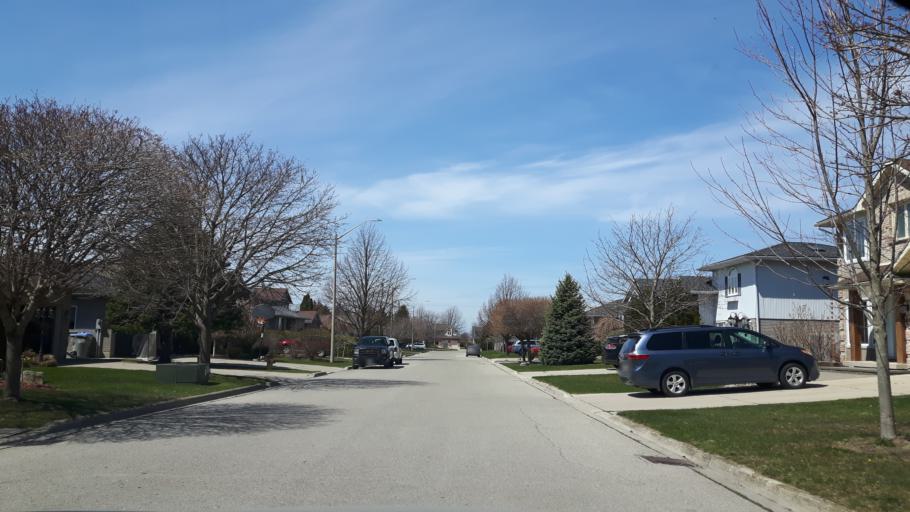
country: CA
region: Ontario
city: Goderich
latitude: 43.7285
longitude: -81.7132
